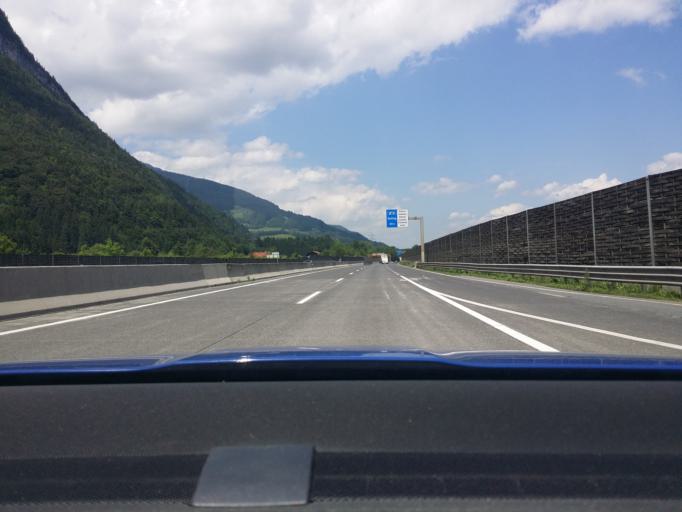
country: AT
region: Salzburg
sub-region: Politischer Bezirk Hallein
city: Golling an der Salzach
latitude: 47.5851
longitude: 13.1563
